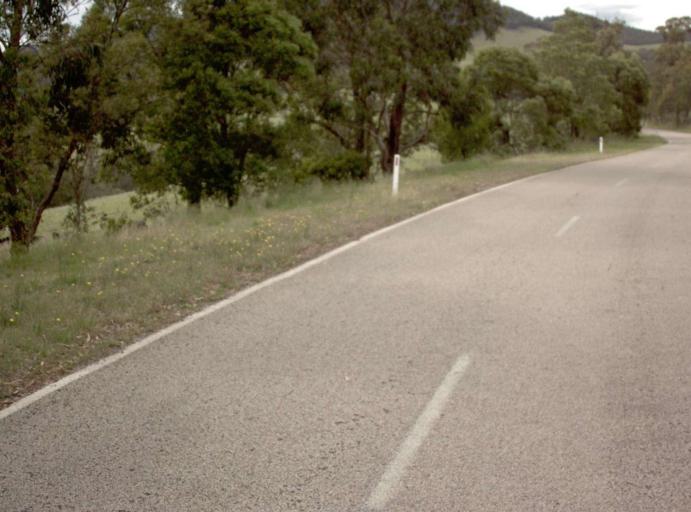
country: AU
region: Victoria
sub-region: East Gippsland
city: Bairnsdale
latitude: -37.5777
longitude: 147.1830
